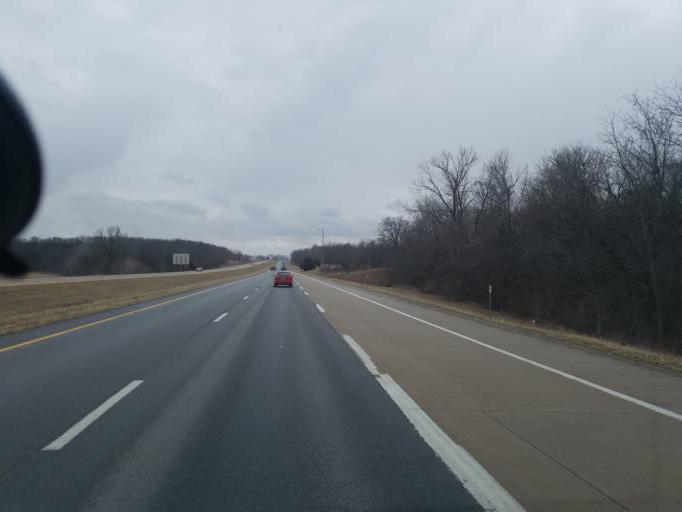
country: US
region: Missouri
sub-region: Randolph County
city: Moberly
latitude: 39.3905
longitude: -92.4133
